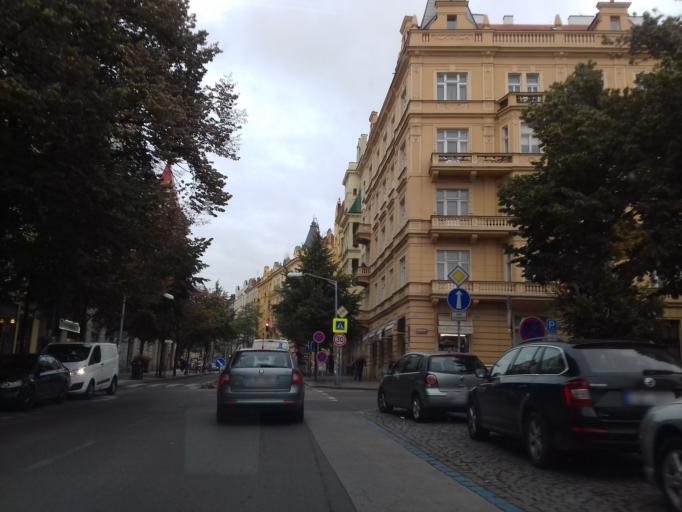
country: CZ
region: Praha
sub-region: Praha 8
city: Karlin
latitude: 50.0781
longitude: 14.4487
